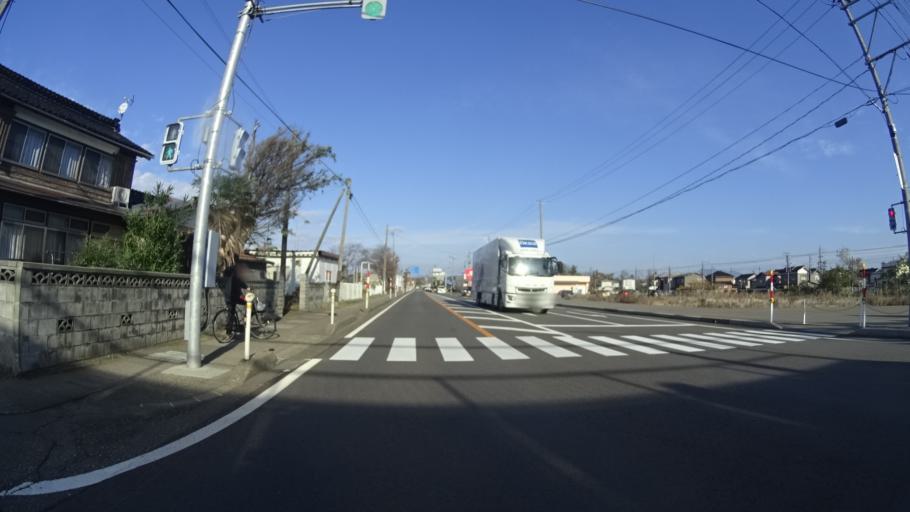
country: JP
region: Niigata
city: Joetsu
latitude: 37.2236
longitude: 138.3250
